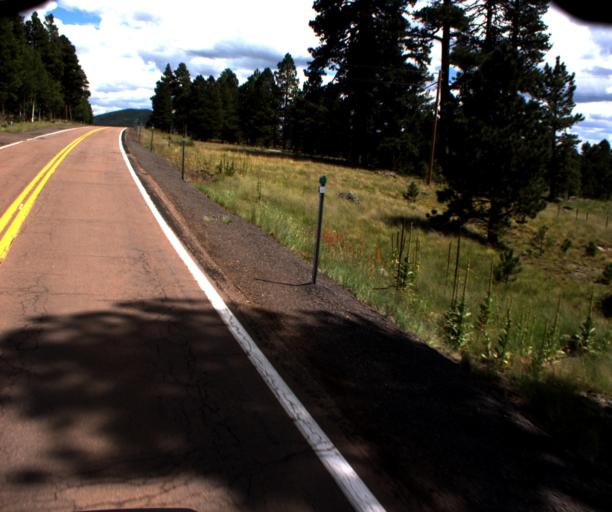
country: US
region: Arizona
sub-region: Apache County
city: Eagar
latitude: 34.0552
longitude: -109.5652
